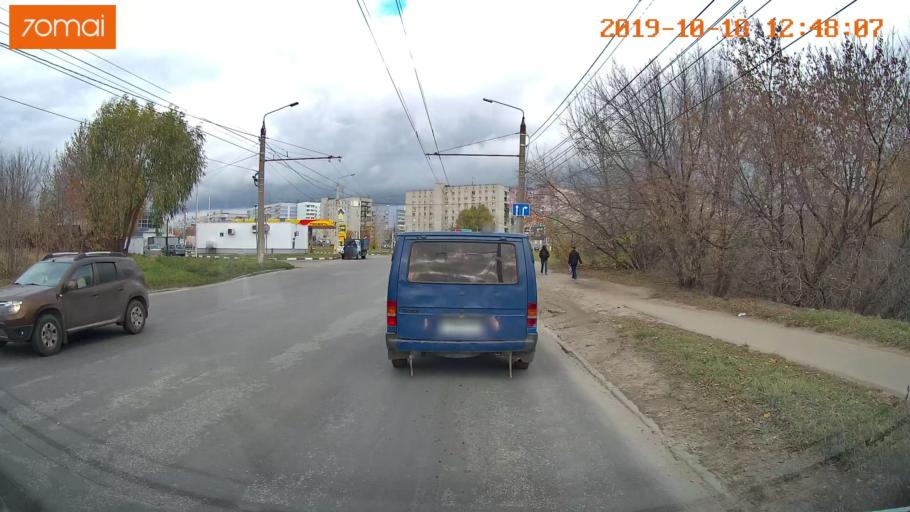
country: RU
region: Rjazan
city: Ryazan'
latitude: 54.6589
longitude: 39.6634
